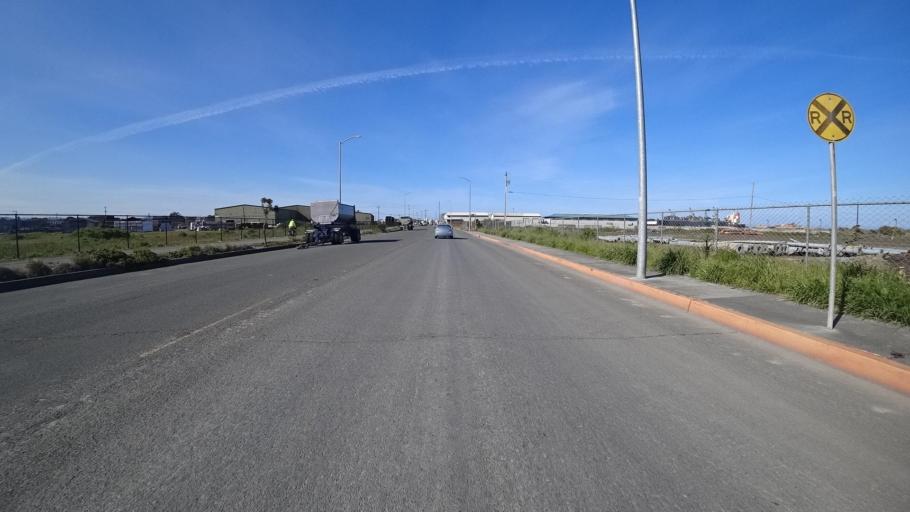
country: US
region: California
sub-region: Humboldt County
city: Eureka
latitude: 40.8004
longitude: -124.1803
